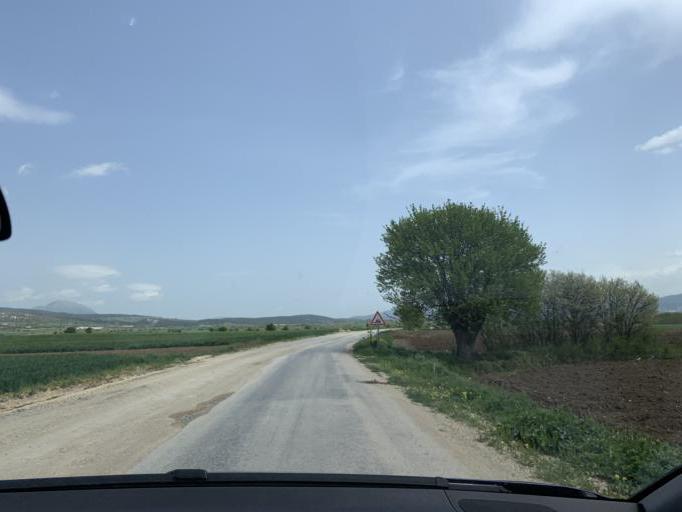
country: TR
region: Bolu
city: Bolu
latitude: 40.7560
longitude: 31.6775
